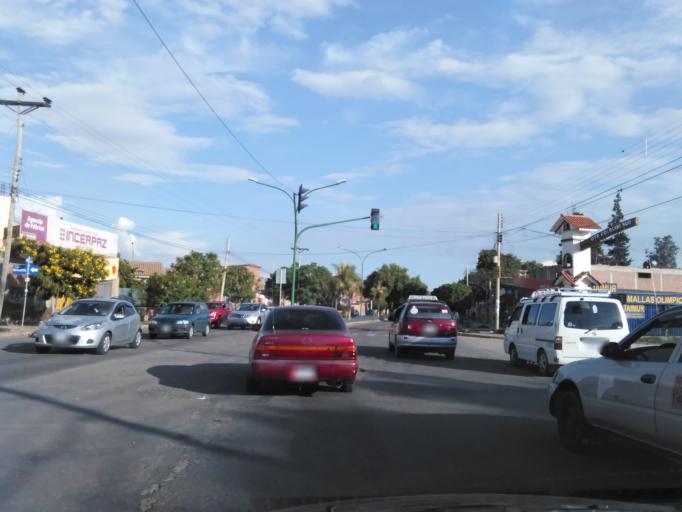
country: BO
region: Cochabamba
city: Cochabamba
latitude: -17.3567
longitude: -66.1849
